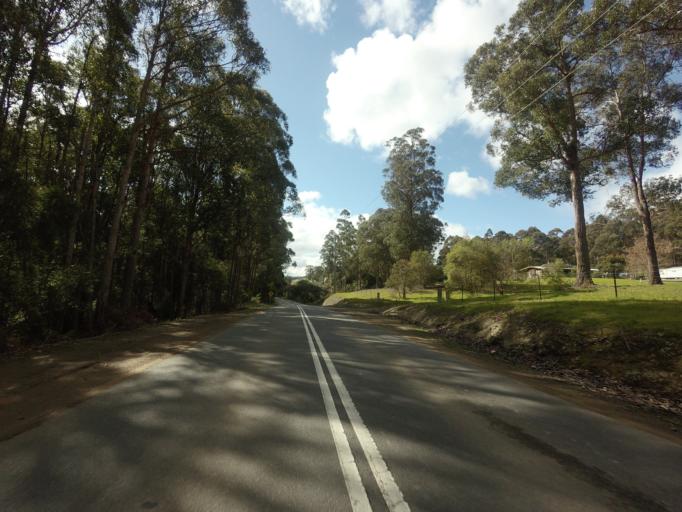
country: AU
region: Tasmania
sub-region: Huon Valley
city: Geeveston
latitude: -43.2242
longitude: 146.9880
